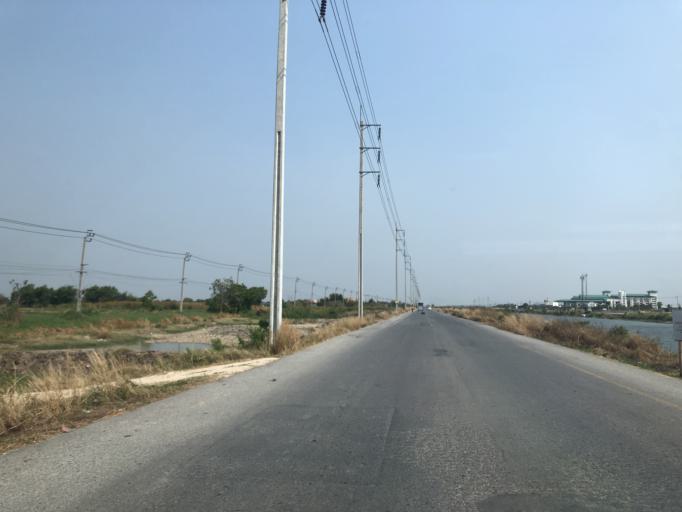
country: TH
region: Samut Prakan
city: Bang Bo District
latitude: 13.5186
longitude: 100.7465
